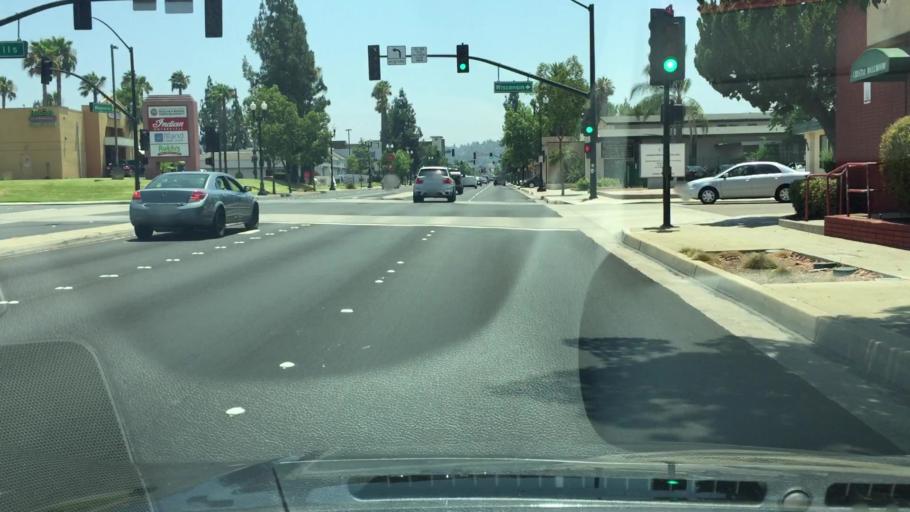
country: US
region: California
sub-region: San Diego County
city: El Cajon
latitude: 32.7995
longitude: -116.9624
